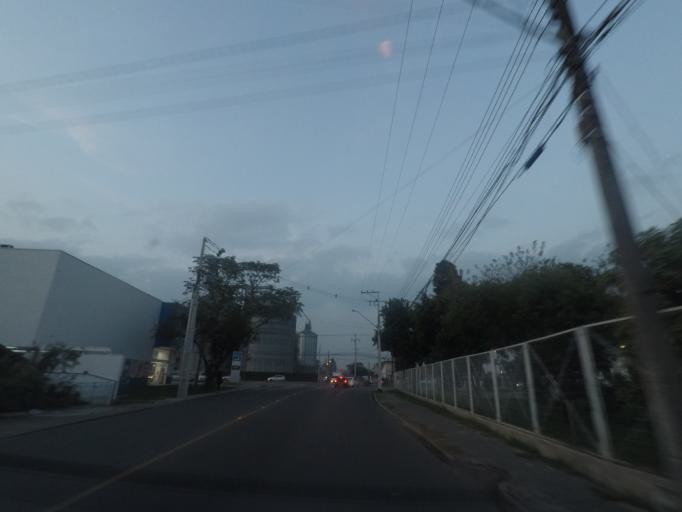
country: BR
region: Parana
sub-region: Pinhais
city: Pinhais
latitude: -25.4481
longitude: -49.1883
